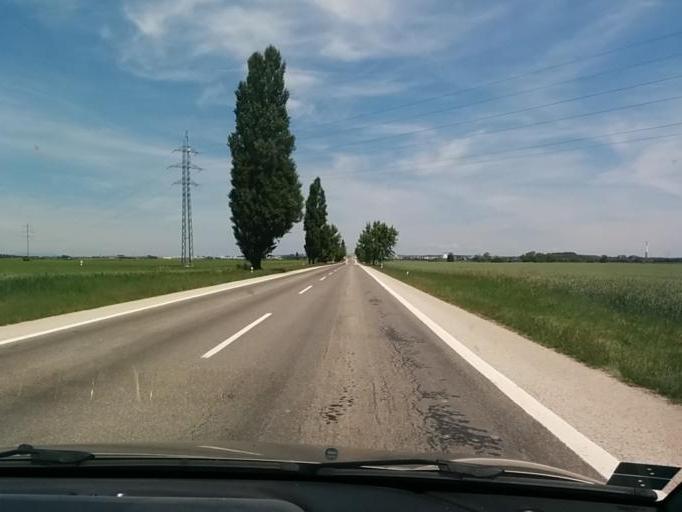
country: SK
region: Trnavsky
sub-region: Okres Galanta
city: Galanta
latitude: 48.2500
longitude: 17.7067
